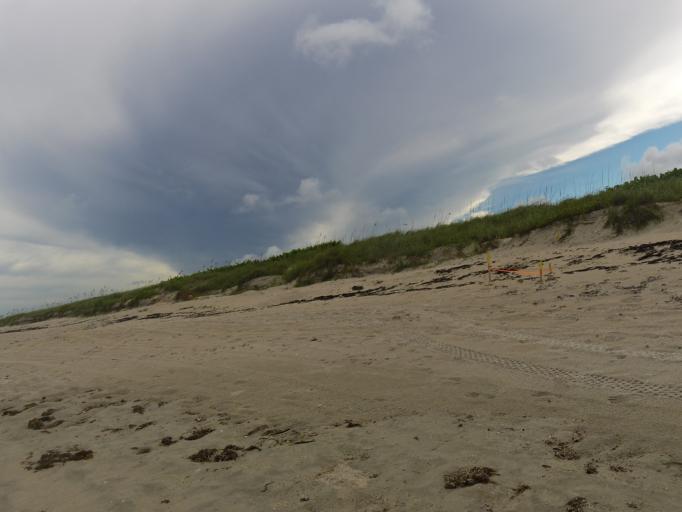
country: US
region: Florida
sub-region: Indian River County
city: Sebastian
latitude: 27.8453
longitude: -80.4395
